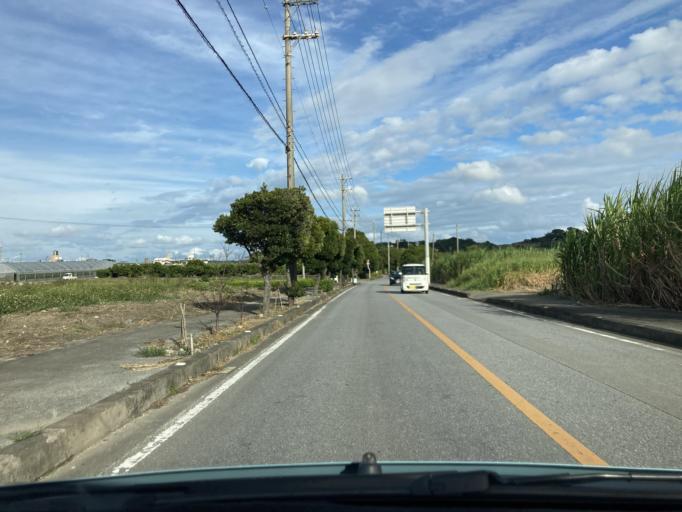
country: JP
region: Okinawa
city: Itoman
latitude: 26.1351
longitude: 127.7126
